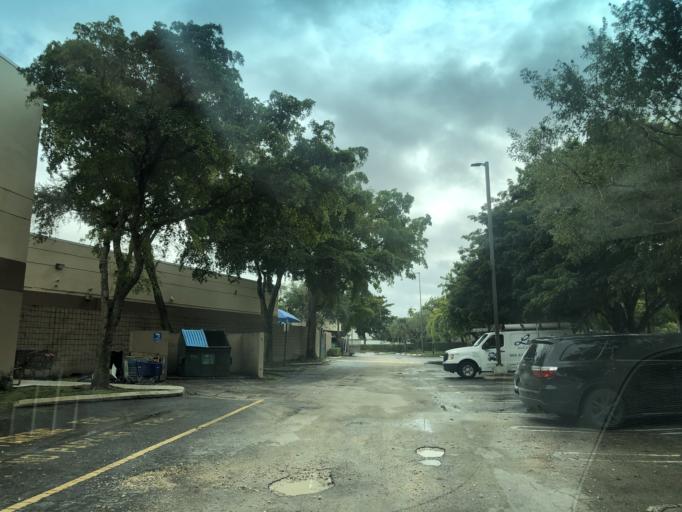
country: US
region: Florida
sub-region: Broward County
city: Tamarac
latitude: 26.2423
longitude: -80.2449
